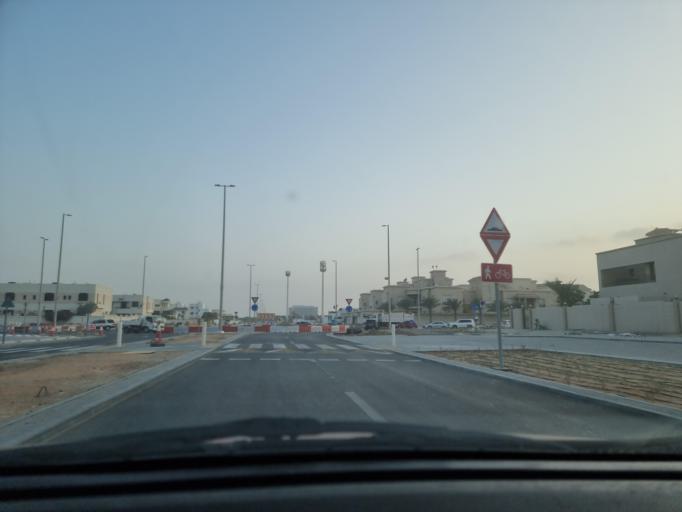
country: AE
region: Abu Dhabi
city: Abu Dhabi
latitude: 24.4089
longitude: 54.5874
